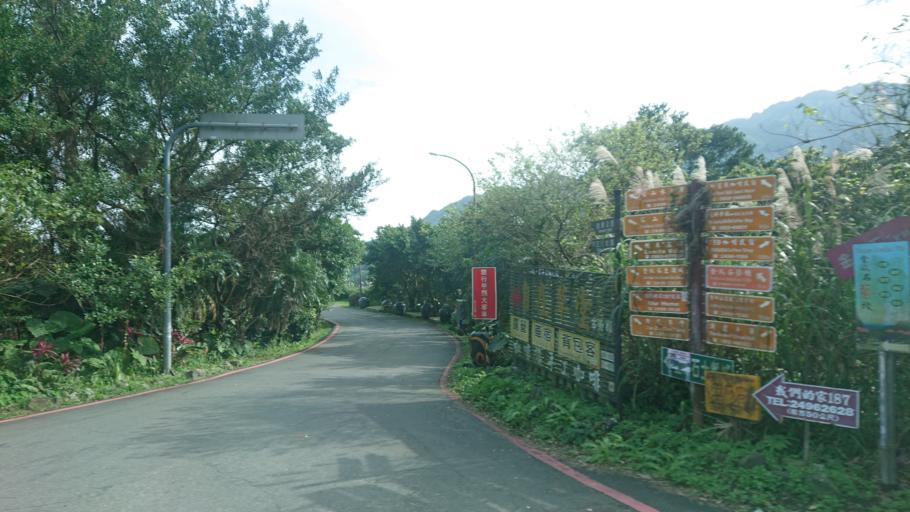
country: TW
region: Taiwan
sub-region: Keelung
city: Keelung
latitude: 25.1093
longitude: 121.8496
